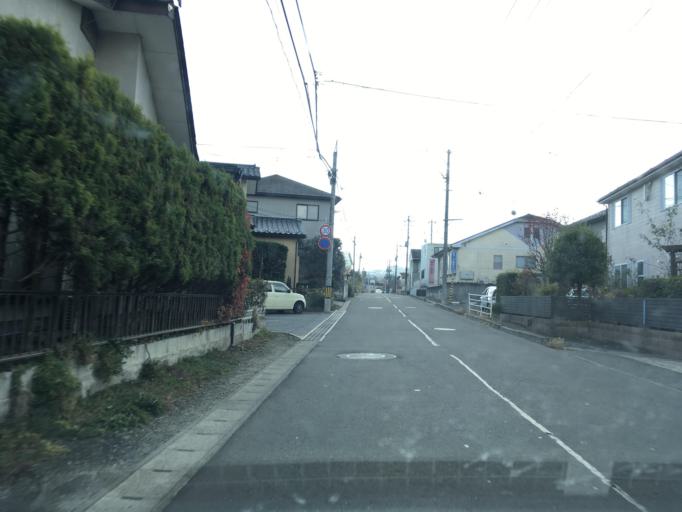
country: JP
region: Miyagi
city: Sendai
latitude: 38.2761
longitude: 140.7645
